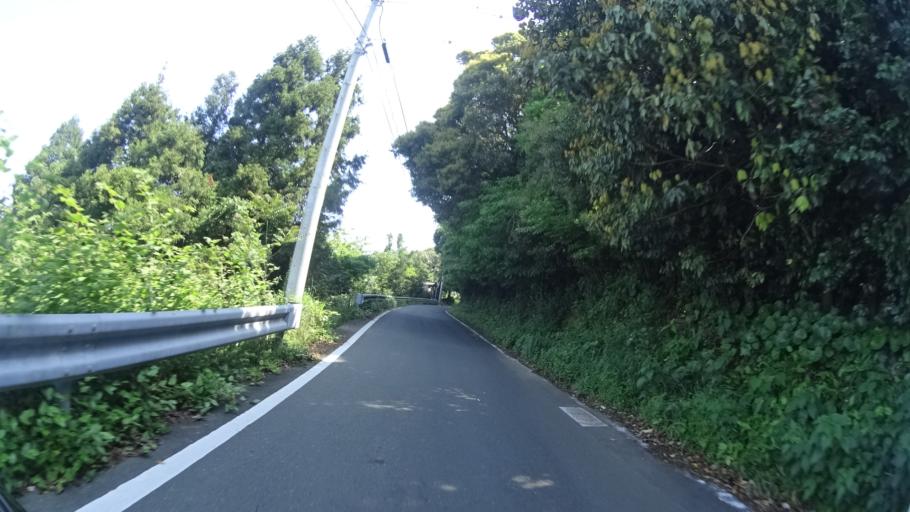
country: JP
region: Ehime
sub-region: Nishiuwa-gun
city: Ikata-cho
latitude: 33.3747
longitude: 132.0562
